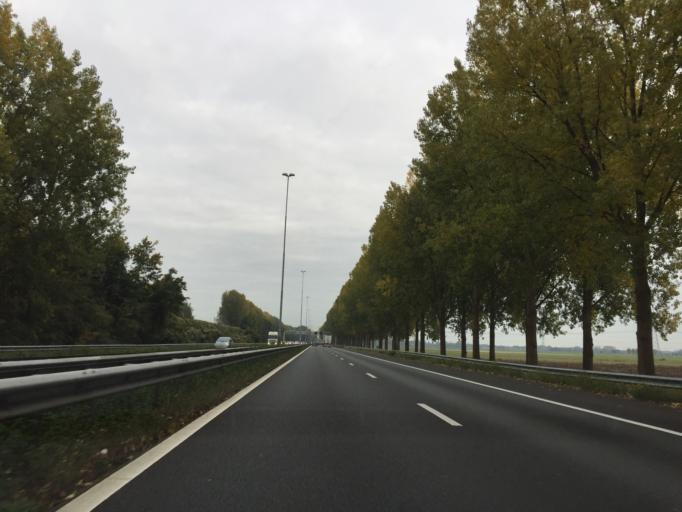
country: NL
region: North Brabant
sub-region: Gemeente Oosterhout
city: Oosterhout
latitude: 51.6618
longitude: 4.8810
